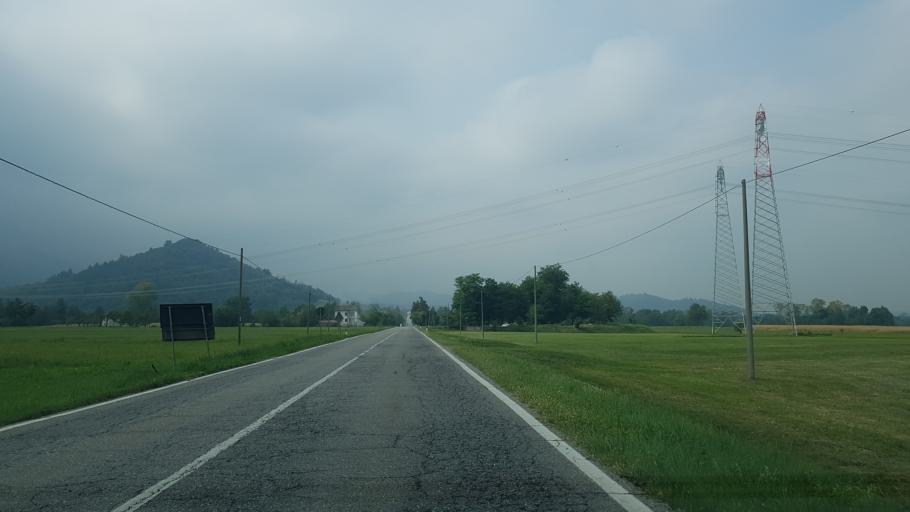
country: IT
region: Piedmont
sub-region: Provincia di Cuneo
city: Chiusa di Pesio
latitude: 44.3299
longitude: 7.6650
